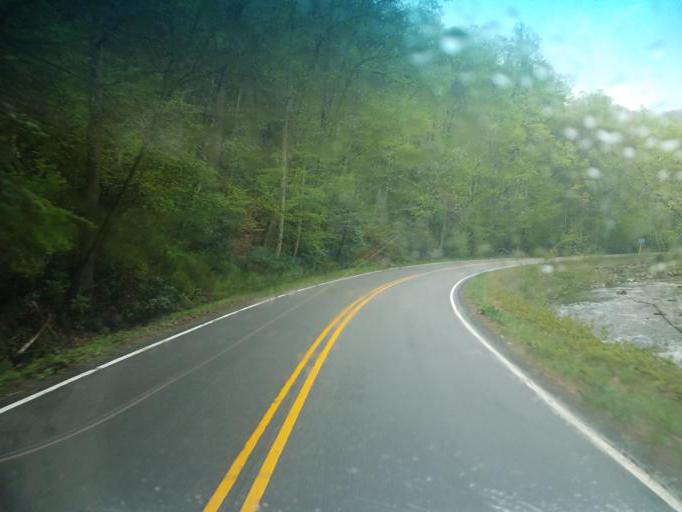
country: US
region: Virginia
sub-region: Washington County
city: Glade Spring
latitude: 36.6324
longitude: -81.7538
